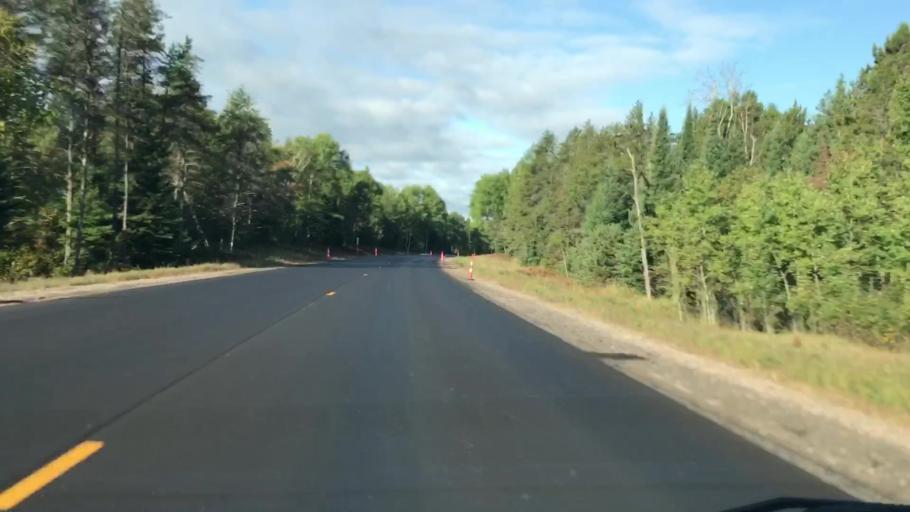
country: US
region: Michigan
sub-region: Mackinac County
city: Saint Ignace
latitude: 46.3462
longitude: -84.9215
